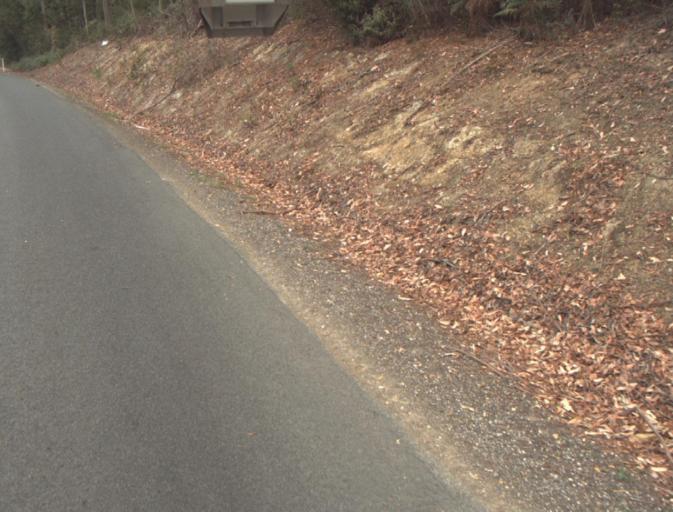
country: AU
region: Tasmania
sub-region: Launceston
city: Mayfield
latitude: -41.2124
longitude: 147.2123
